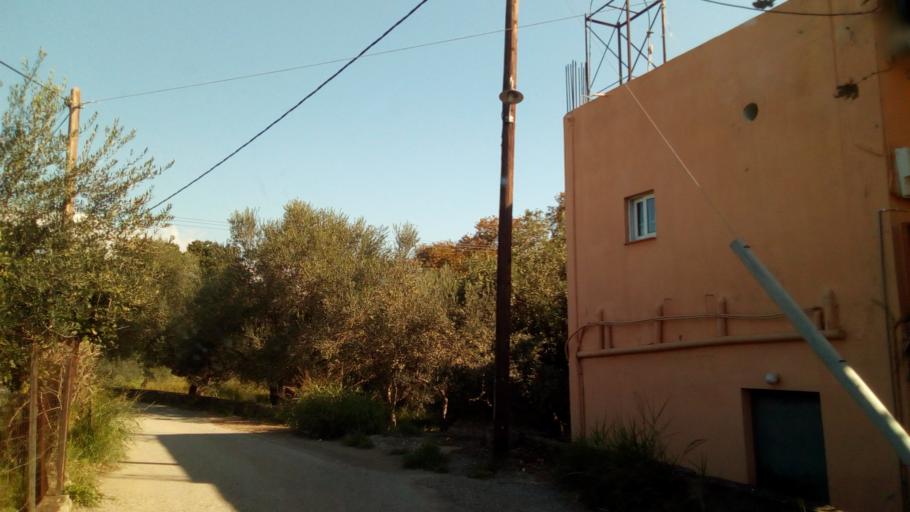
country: GR
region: West Greece
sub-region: Nomos Aitolias kai Akarnanias
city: Antirrio
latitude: 38.3419
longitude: 21.7304
